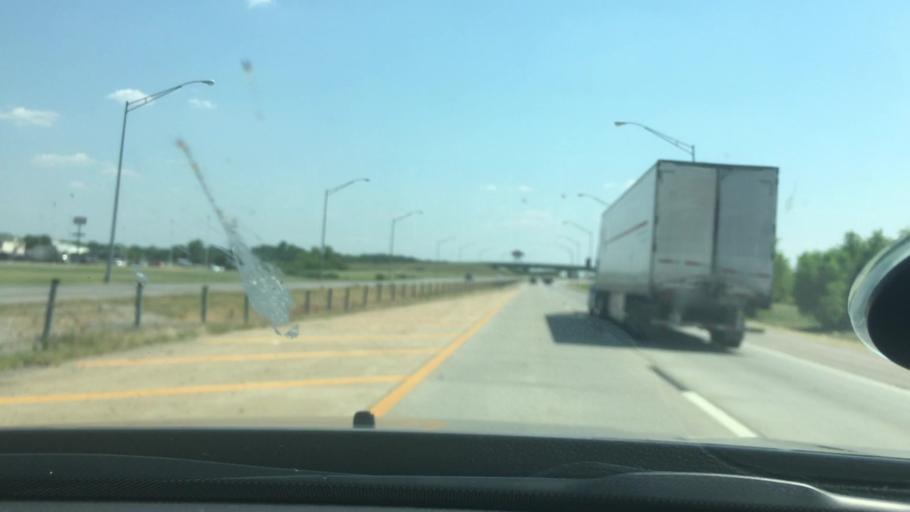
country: US
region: Oklahoma
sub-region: Bryan County
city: Calera
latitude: 33.9518
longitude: -96.4167
